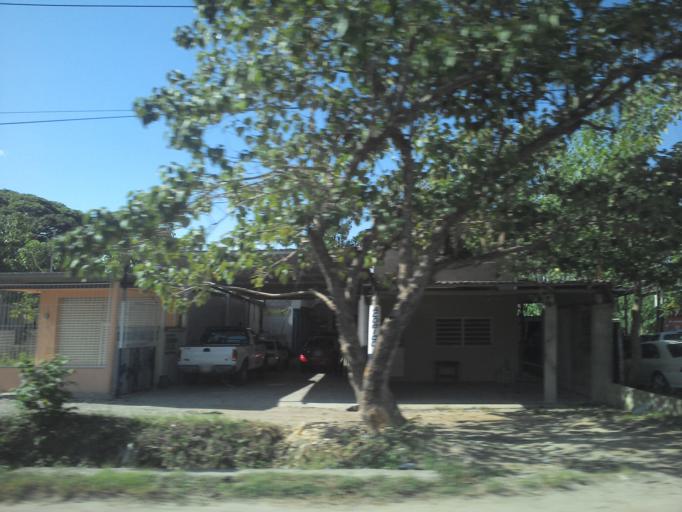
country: MX
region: Chiapas
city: Palenque
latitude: 17.5427
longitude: -91.9884
